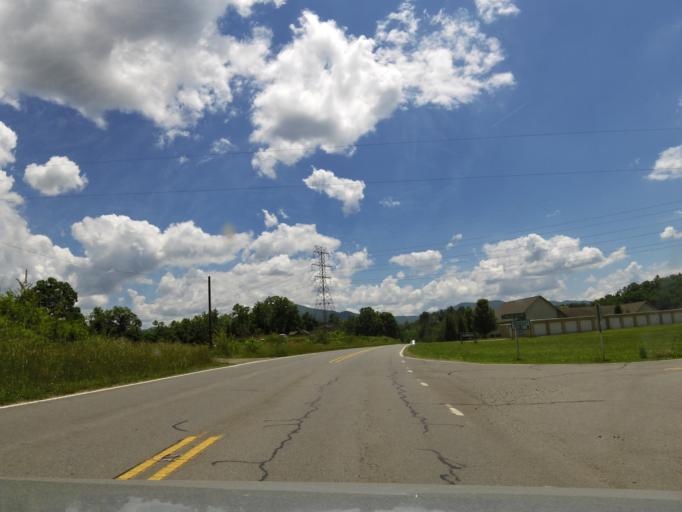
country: US
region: North Carolina
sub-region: Graham County
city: Robbinsville
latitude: 35.3372
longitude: -83.8123
